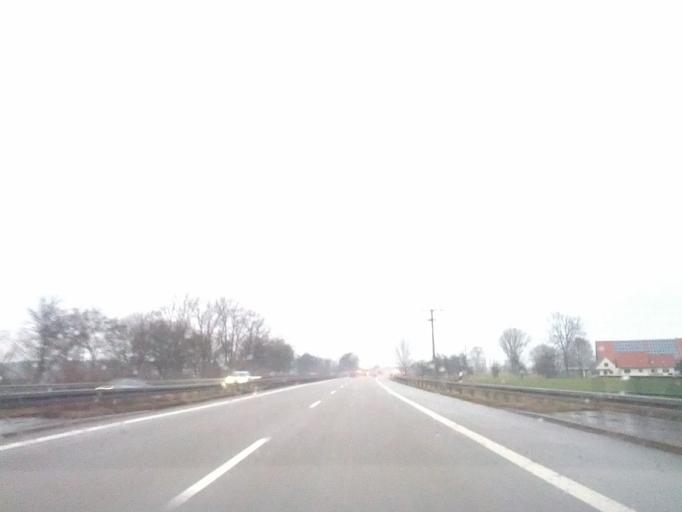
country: DE
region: Bavaria
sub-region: Swabia
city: Woringen
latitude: 47.9377
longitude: 10.2014
